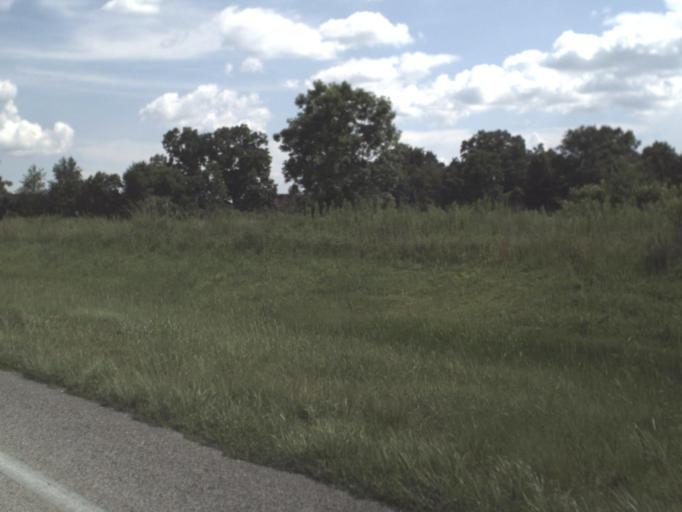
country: US
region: Florida
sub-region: Alachua County
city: Hawthorne
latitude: 29.6171
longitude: -82.0958
